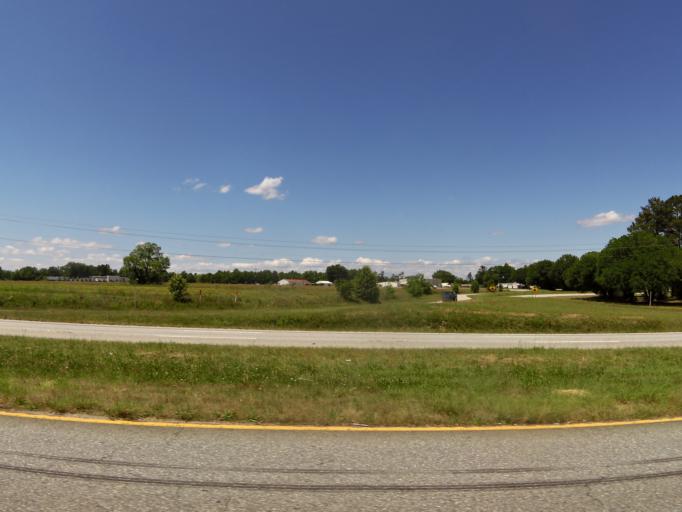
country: US
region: South Carolina
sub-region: Aiken County
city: Clearwater
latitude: 33.4884
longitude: -81.9226
